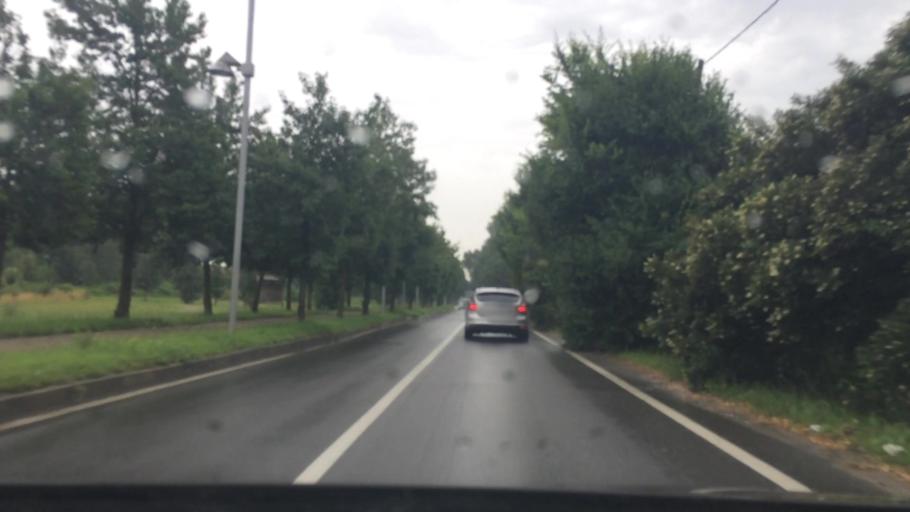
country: IT
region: Lombardy
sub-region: Citta metropolitana di Milano
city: Pero
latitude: 45.5089
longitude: 9.0739
